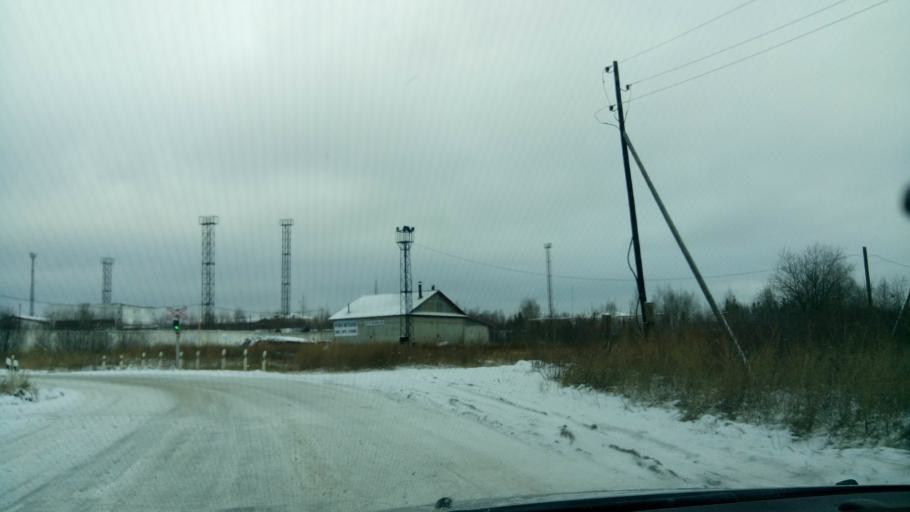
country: RU
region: Sverdlovsk
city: Polevskoy
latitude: 56.4633
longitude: 60.1825
